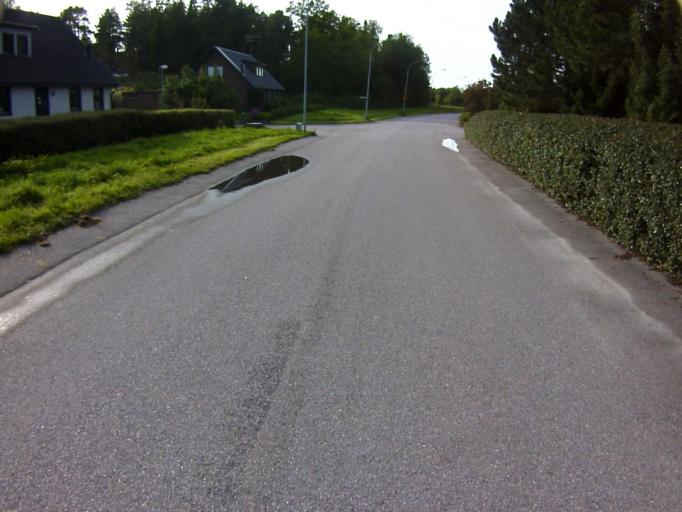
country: SE
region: Soedermanland
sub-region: Eskilstuna Kommun
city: Eskilstuna
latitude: 59.3938
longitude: 16.5478
